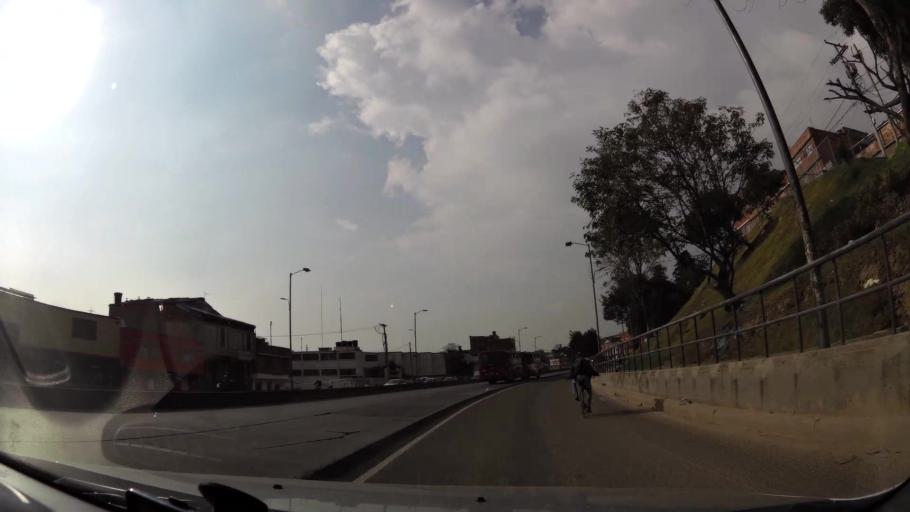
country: CO
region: Bogota D.C.
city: Bogota
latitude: 4.5625
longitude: -74.1248
